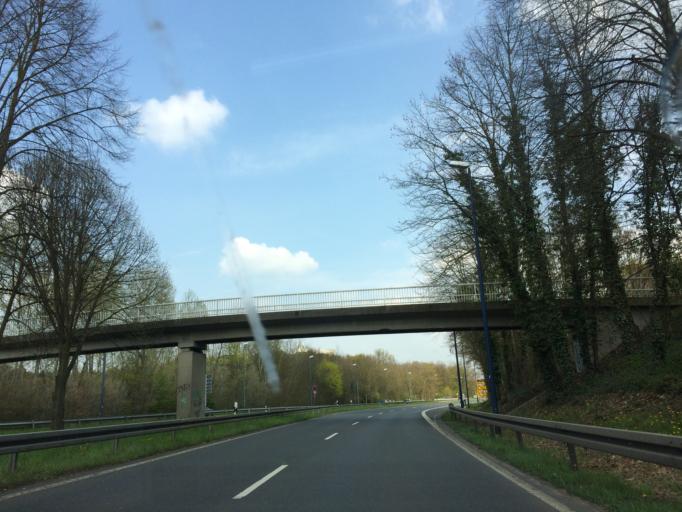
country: DE
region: Hesse
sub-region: Regierungsbezirk Darmstadt
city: Offenbach
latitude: 50.0945
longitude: 8.8013
